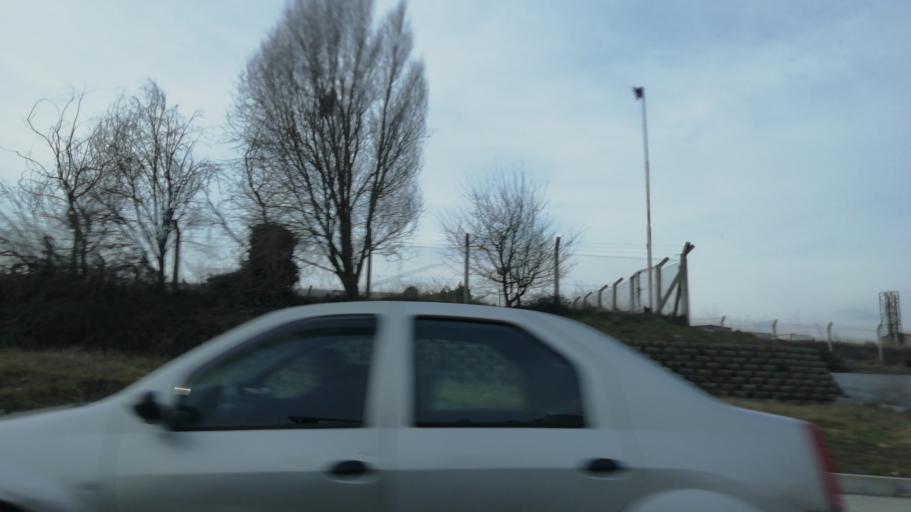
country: TR
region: Istanbul
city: Basaksehir
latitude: 41.1112
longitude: 28.7965
